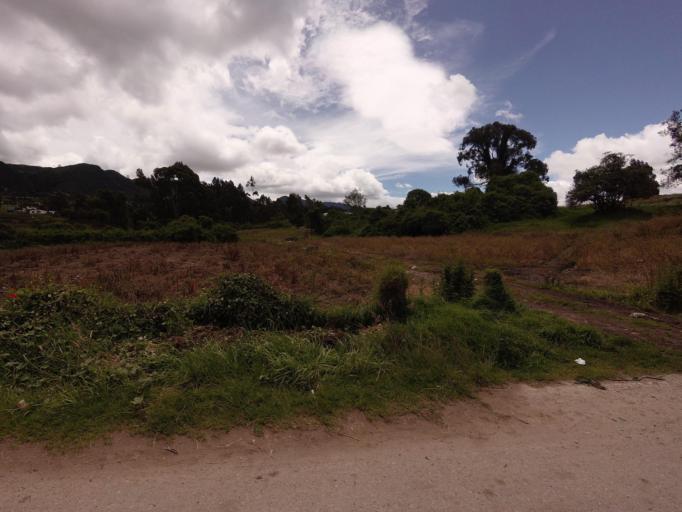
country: CO
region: Cundinamarca
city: Tabio
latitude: 4.9748
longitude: -74.0683
